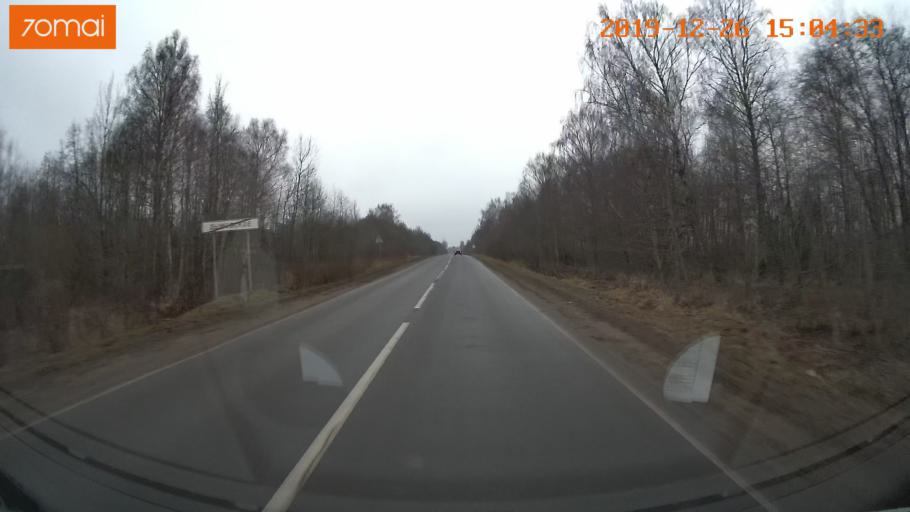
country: RU
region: Jaroslavl
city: Rybinsk
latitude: 58.1986
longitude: 38.8607
